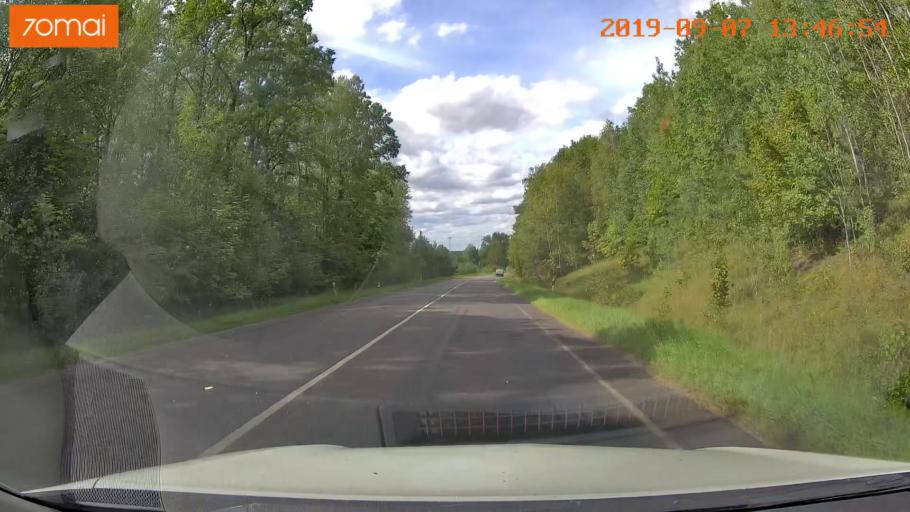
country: LT
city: Baltoji Voke
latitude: 54.5930
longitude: 25.2233
